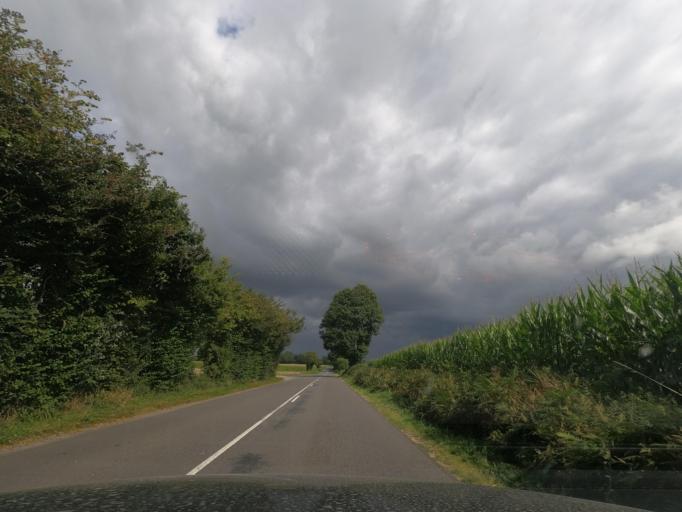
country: FR
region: Lower Normandy
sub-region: Departement de l'Orne
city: Briouze
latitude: 48.6917
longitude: -0.4289
